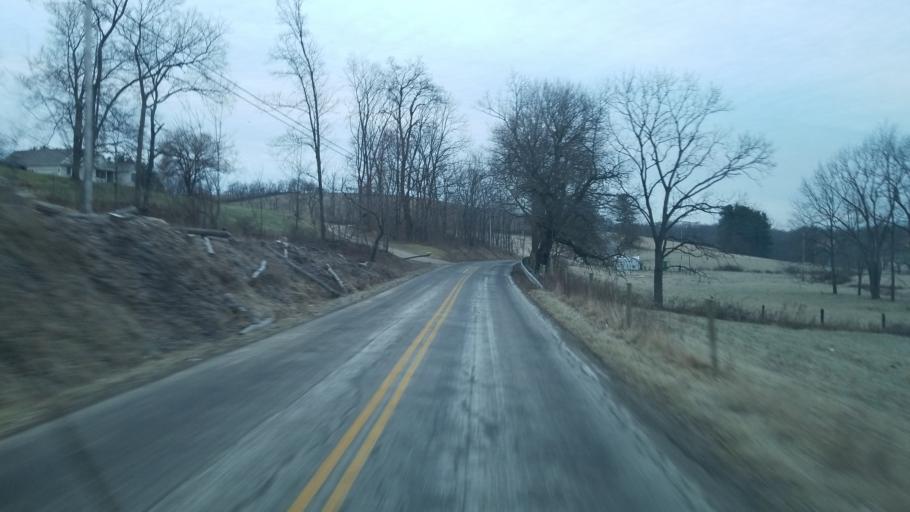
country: US
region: Ohio
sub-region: Holmes County
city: Millersburg
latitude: 40.4973
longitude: -81.8819
